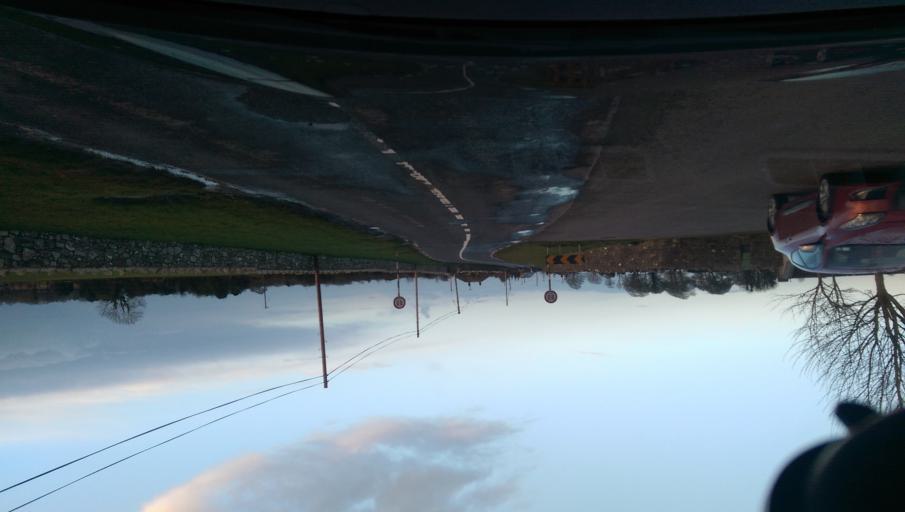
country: IE
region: Connaught
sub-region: County Galway
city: Ballinasloe
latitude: 53.3947
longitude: -8.3280
